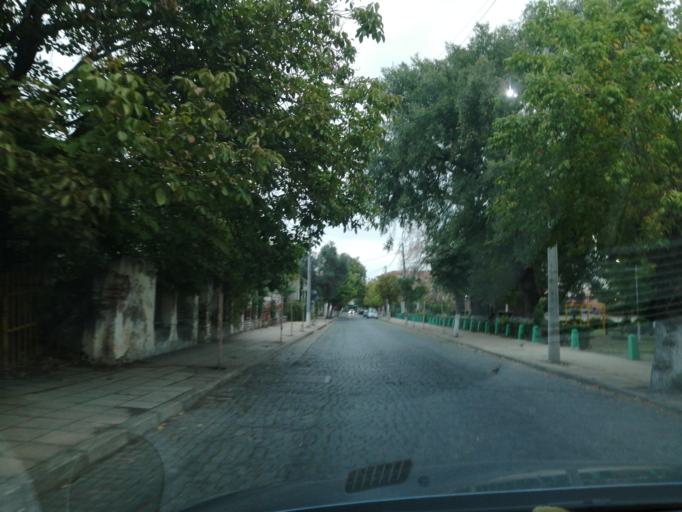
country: MK
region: Gevgelija
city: Gevgelija
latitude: 41.1424
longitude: 22.5098
